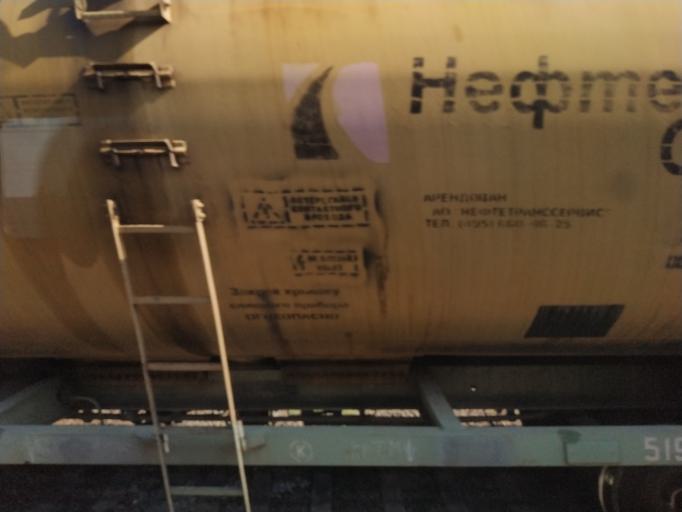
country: RU
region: Volgograd
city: Gumrak
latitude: 48.7806
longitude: 44.3768
